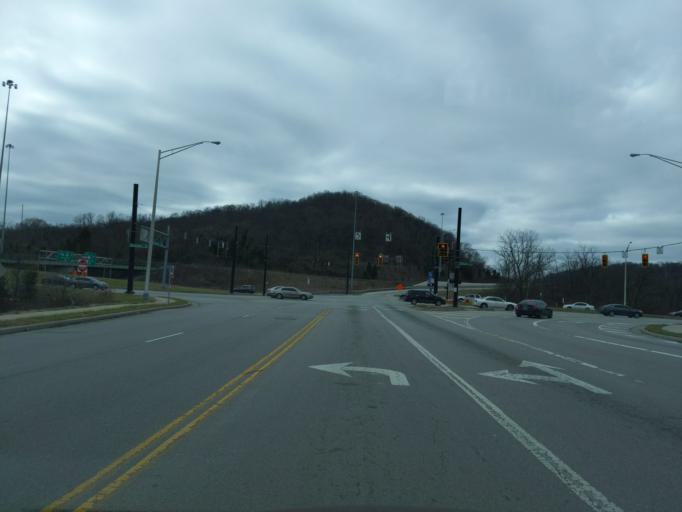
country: US
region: Ohio
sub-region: Hamilton County
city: Finneytown
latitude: 39.1627
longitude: -84.5509
